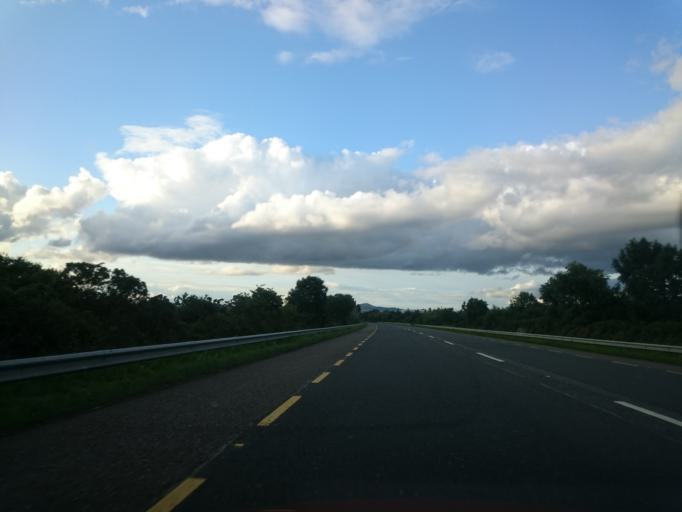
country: IE
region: Leinster
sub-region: Loch Garman
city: Enniscorthy
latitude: 52.5317
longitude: -6.5557
